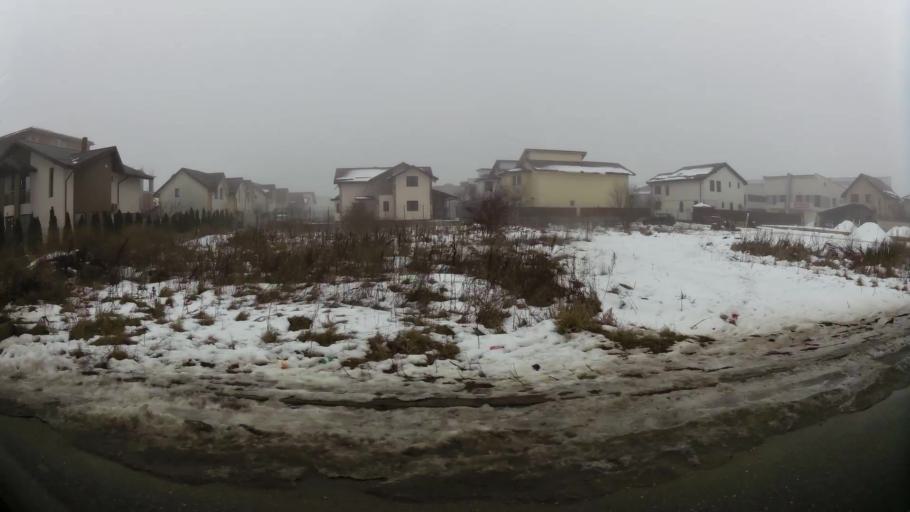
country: RO
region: Ilfov
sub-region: Comuna Chiajna
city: Chiajna
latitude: 44.4523
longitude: 25.9779
